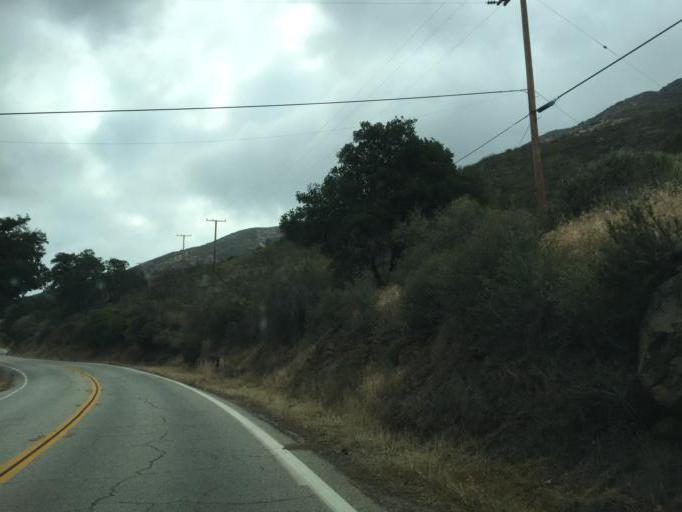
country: US
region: California
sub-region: Los Angeles County
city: Green Valley
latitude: 34.5600
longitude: -118.4040
